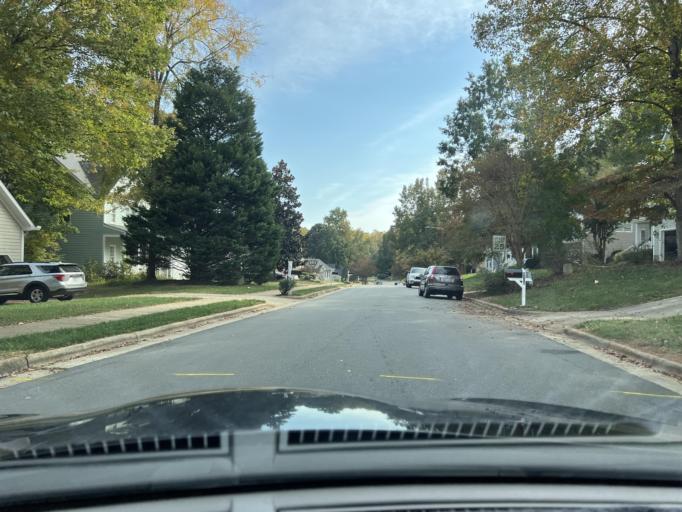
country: US
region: North Carolina
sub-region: Wake County
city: Wake Forest
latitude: 35.8976
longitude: -78.5833
